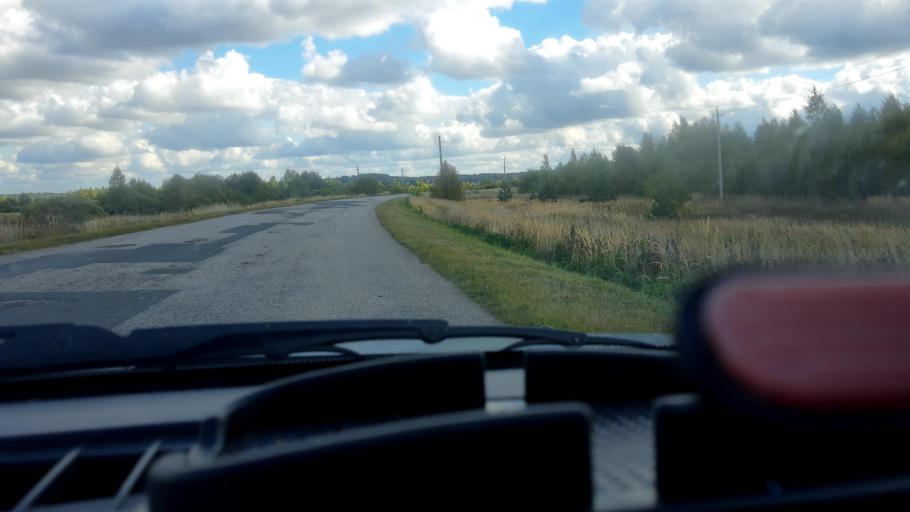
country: RU
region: Mariy-El
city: Kilemary
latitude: 56.9421
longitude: 46.6812
